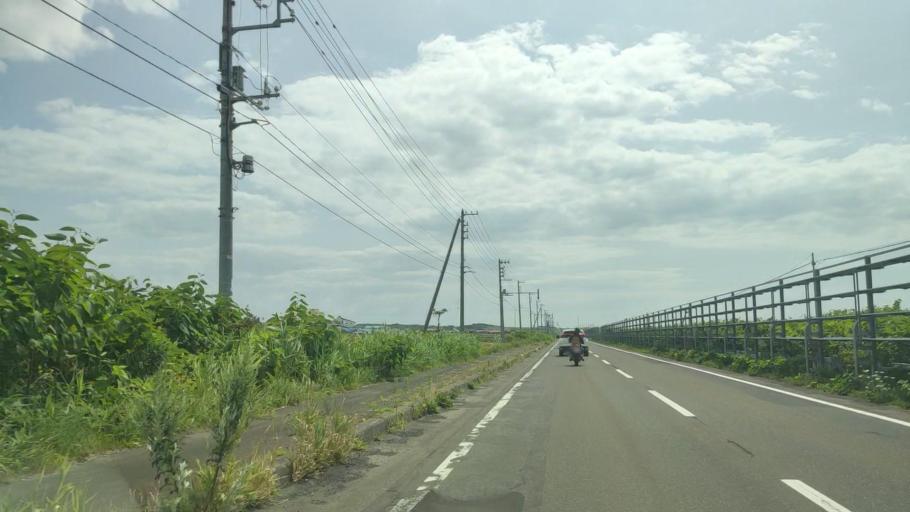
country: JP
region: Hokkaido
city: Rumoi
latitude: 44.4554
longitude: 141.7596
